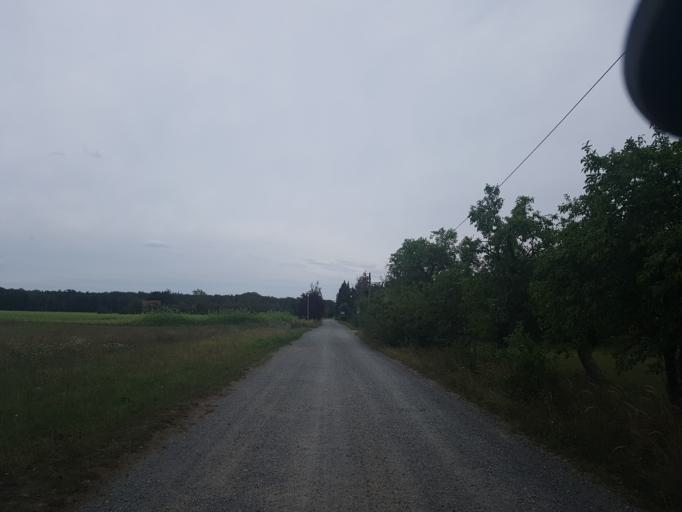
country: DE
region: Brandenburg
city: Finsterwalde
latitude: 51.6091
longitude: 13.6480
